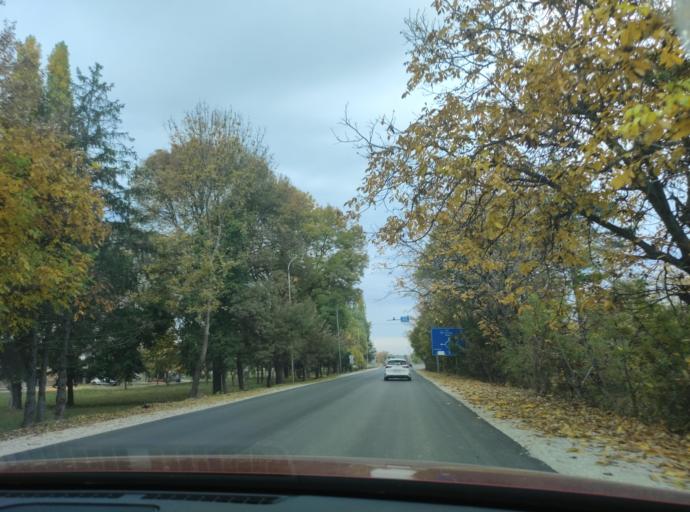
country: BG
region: Montana
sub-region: Obshtina Montana
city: Montana
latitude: 43.4000
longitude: 23.2402
